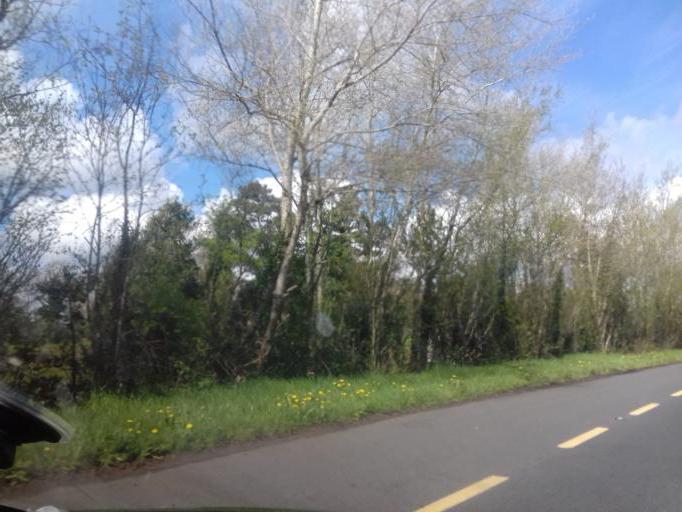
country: IE
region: Ulster
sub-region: An Cabhan
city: Belturbet
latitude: 54.1056
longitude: -7.4678
